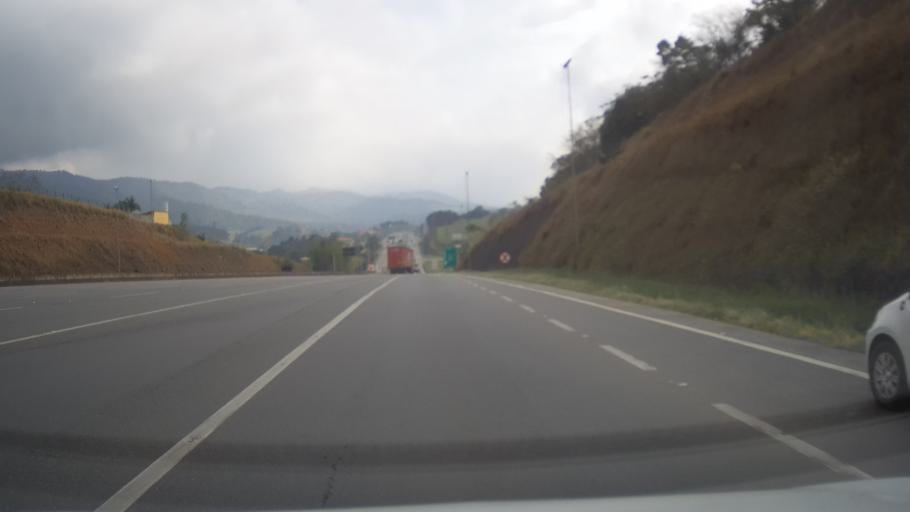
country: BR
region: Minas Gerais
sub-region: Extrema
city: Extrema
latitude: -22.9079
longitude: -46.4238
